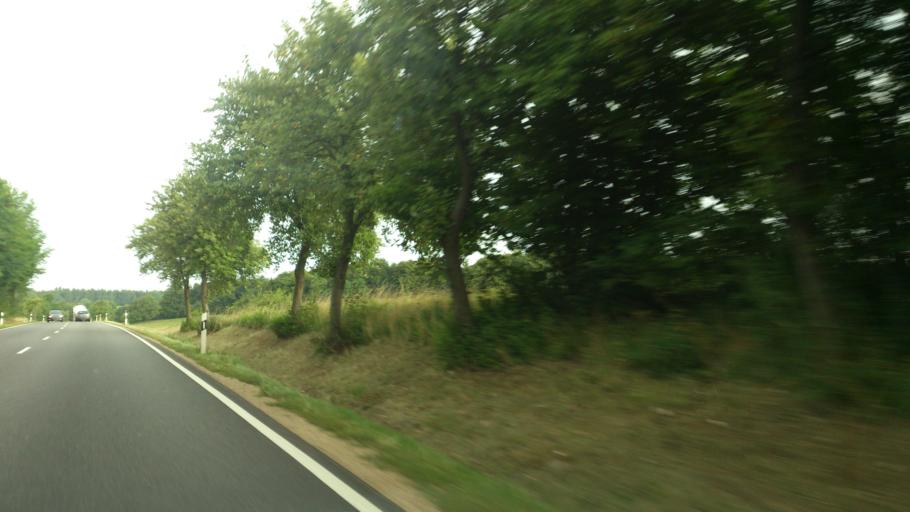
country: DE
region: Rheinland-Pfalz
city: Ohlenhard
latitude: 50.4426
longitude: 6.7193
